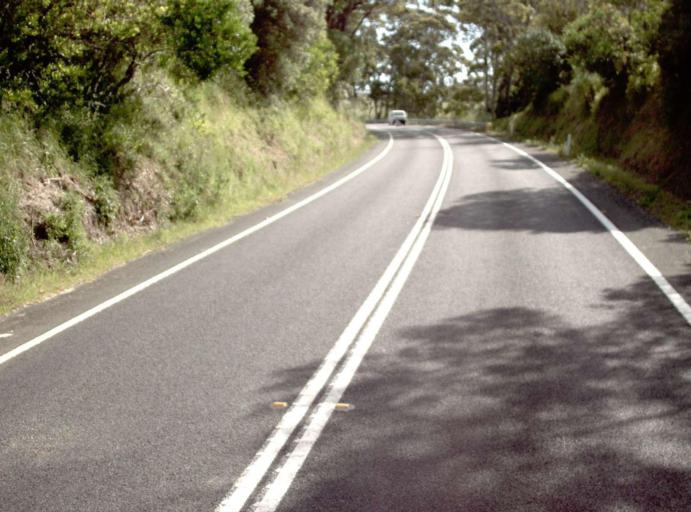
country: AU
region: Victoria
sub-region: East Gippsland
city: Lakes Entrance
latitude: -37.8539
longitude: 148.0327
